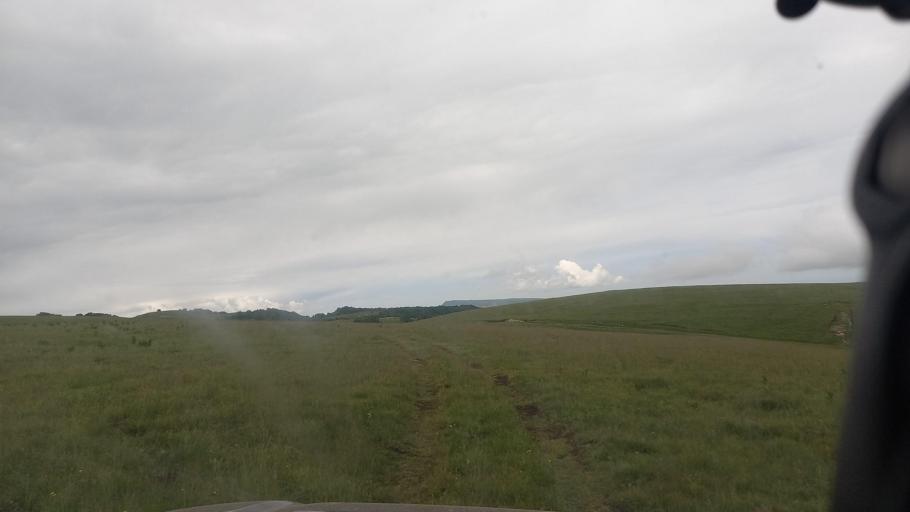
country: RU
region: Karachayevo-Cherkesiya
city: Pregradnaya
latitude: 43.9803
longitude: 41.2980
